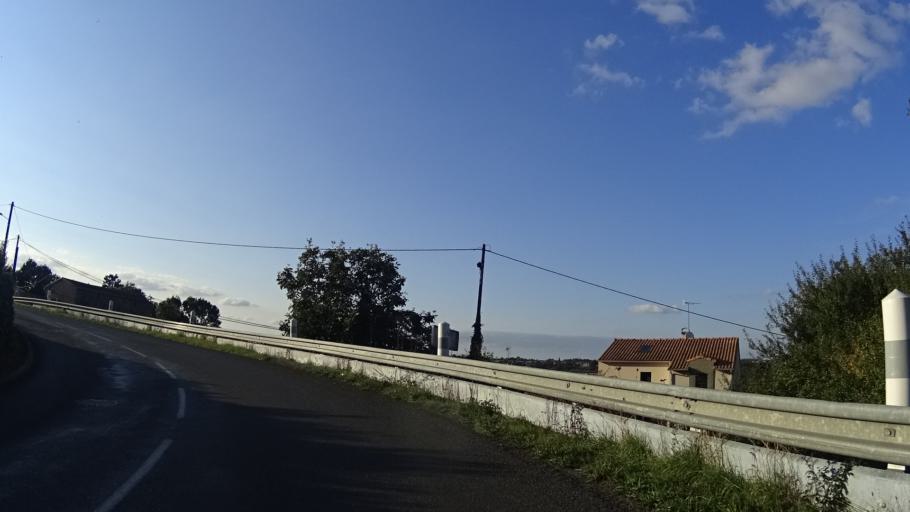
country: FR
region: Pays de la Loire
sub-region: Departement de Maine-et-Loire
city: Champtoceaux
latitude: 47.3377
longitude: -1.2580
